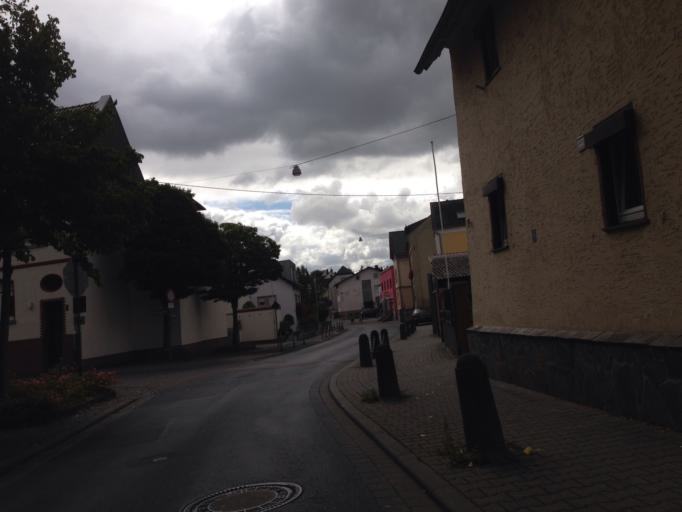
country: DE
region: Hesse
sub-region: Regierungsbezirk Giessen
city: Elz
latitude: 50.4178
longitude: 8.0599
